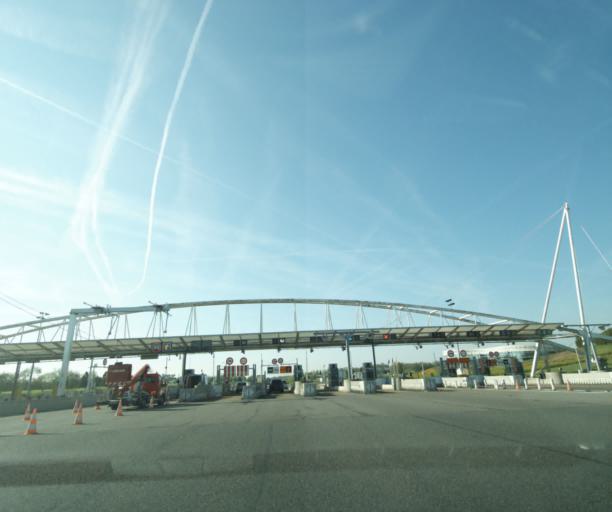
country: FR
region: Ile-de-France
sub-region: Departement de Seine-et-Marne
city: Souppes-sur-Loing
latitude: 48.1768
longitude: 2.7667
